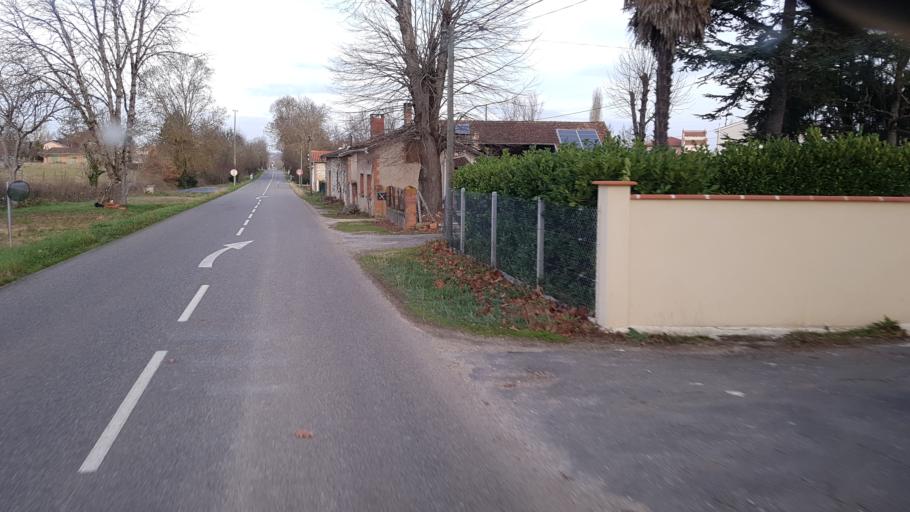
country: FR
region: Midi-Pyrenees
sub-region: Departement du Tarn-et-Garonne
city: Caussade
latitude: 44.1499
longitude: 1.5532
